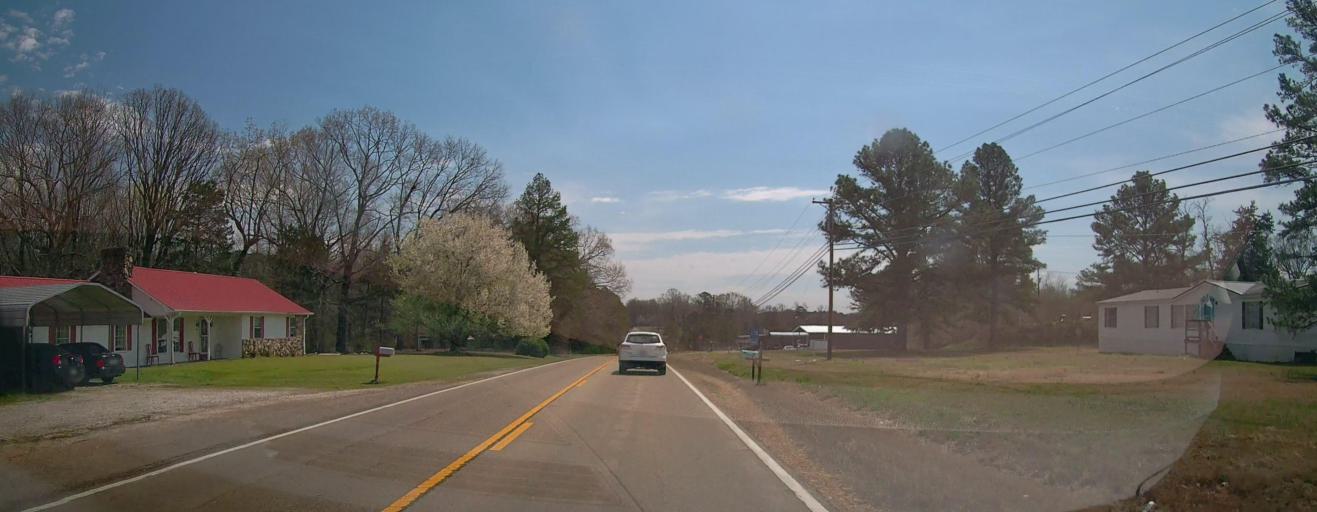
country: US
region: Mississippi
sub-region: Union County
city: New Albany
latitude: 34.4532
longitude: -88.9729
